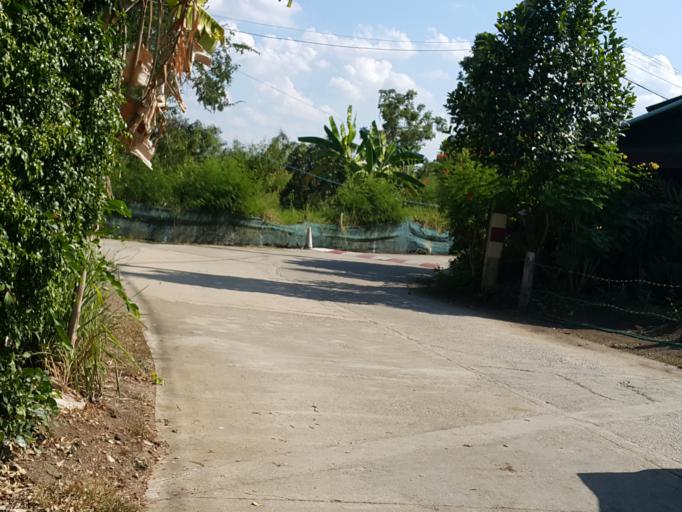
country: TH
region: Chiang Mai
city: San Kamphaeng
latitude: 18.8019
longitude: 99.0982
